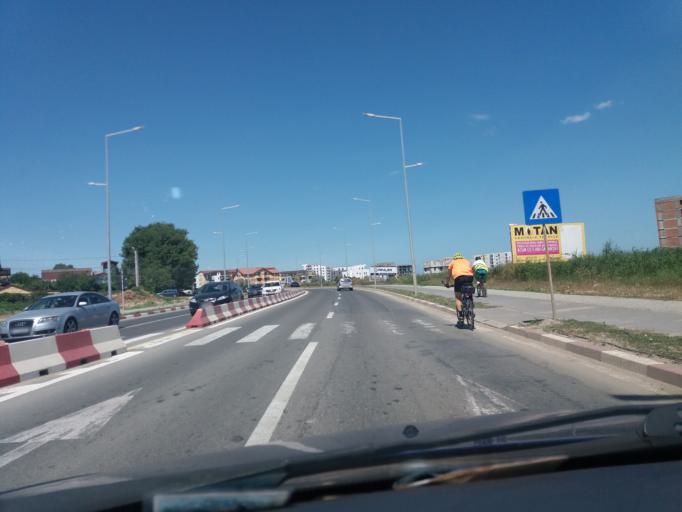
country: RO
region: Constanta
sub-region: Comuna Navodari
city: Navodari
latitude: 44.2893
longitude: 28.6178
